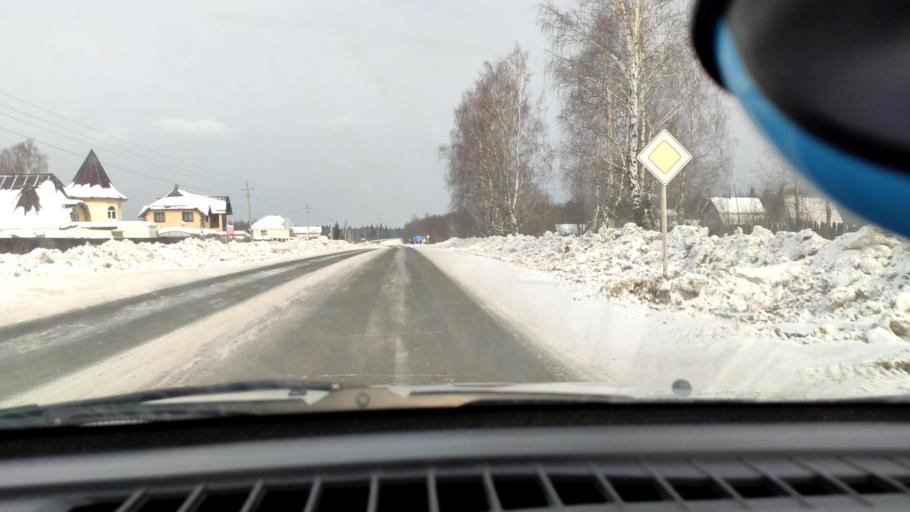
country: RU
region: Perm
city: Krasnokamsk
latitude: 58.0973
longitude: 55.8086
